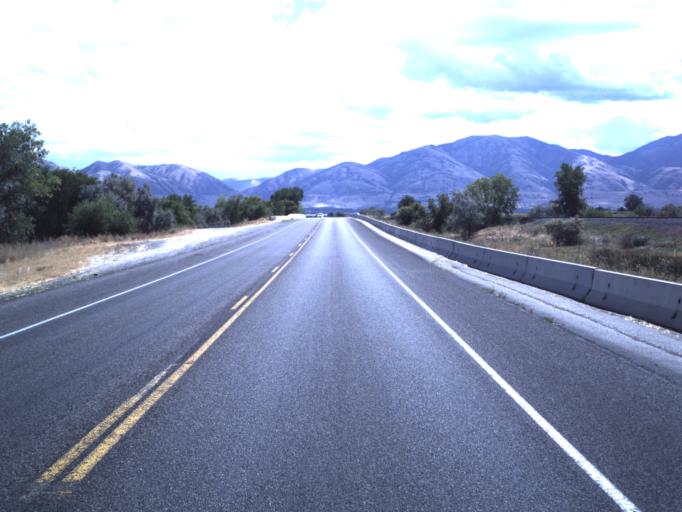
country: US
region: Utah
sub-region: Box Elder County
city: Brigham City
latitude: 41.5467
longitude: -112.0981
